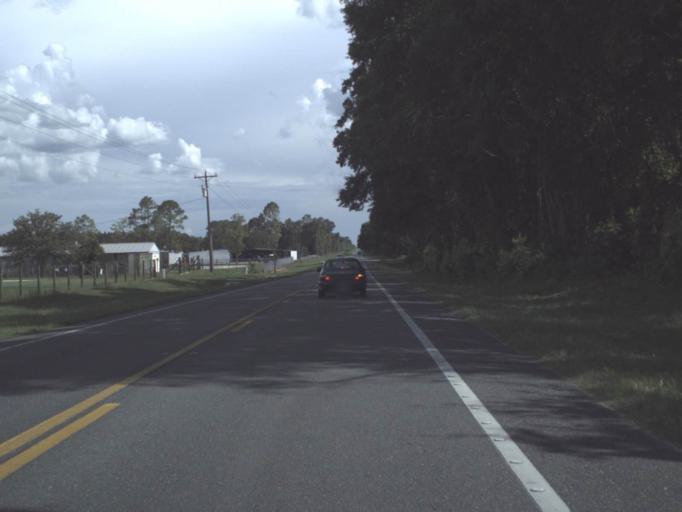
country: US
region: Florida
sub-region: Gilchrist County
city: Trenton
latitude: 29.8242
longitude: -82.8673
